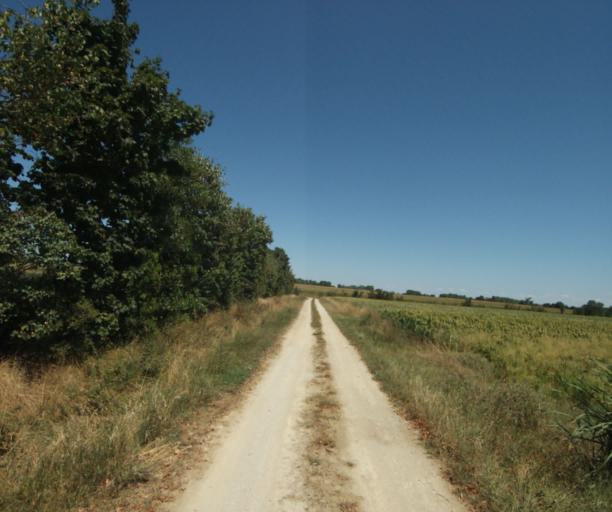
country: FR
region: Midi-Pyrenees
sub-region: Departement de la Haute-Garonne
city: Saint-Felix-Lauragais
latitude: 43.4665
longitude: 1.9392
